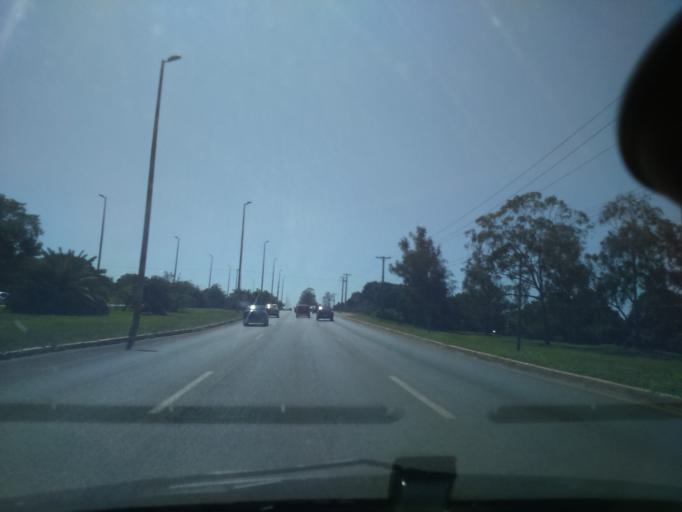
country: BR
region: Federal District
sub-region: Brasilia
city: Brasilia
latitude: -15.8397
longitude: -47.9085
